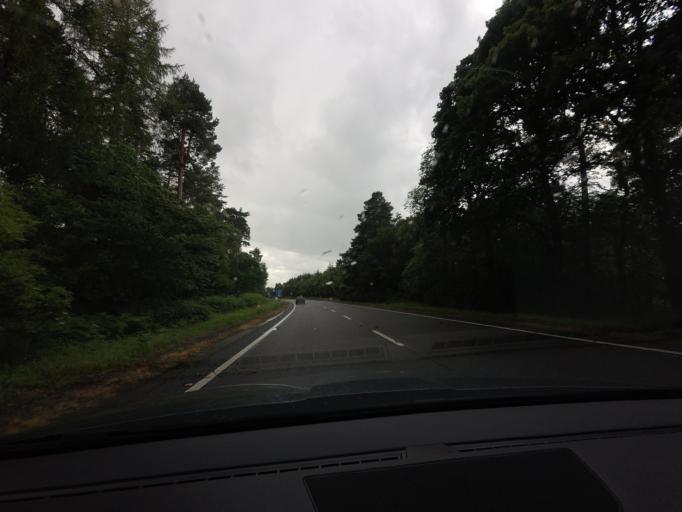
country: GB
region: Scotland
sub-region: Highland
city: Fortrose
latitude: 57.5274
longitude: -4.0567
